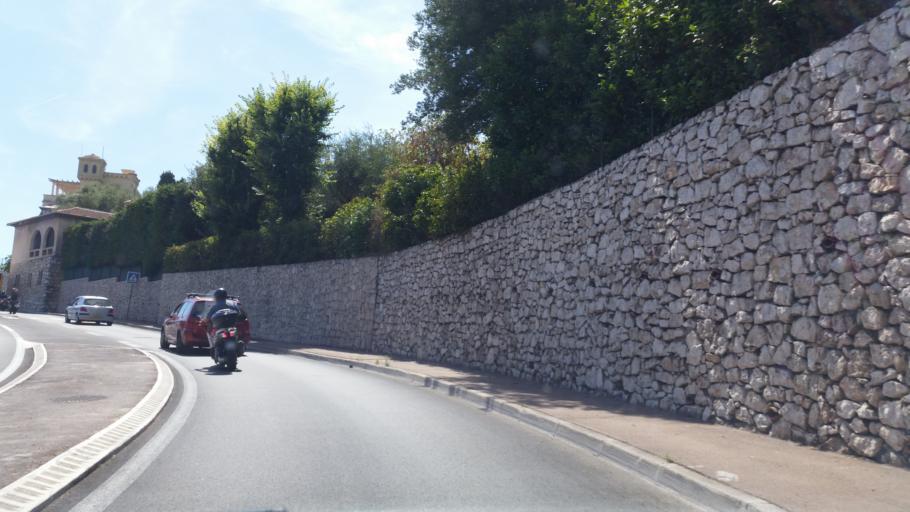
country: FR
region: Provence-Alpes-Cote d'Azur
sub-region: Departement des Alpes-Maritimes
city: Roquebrune-Cap-Martin
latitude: 43.7624
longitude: 7.4706
